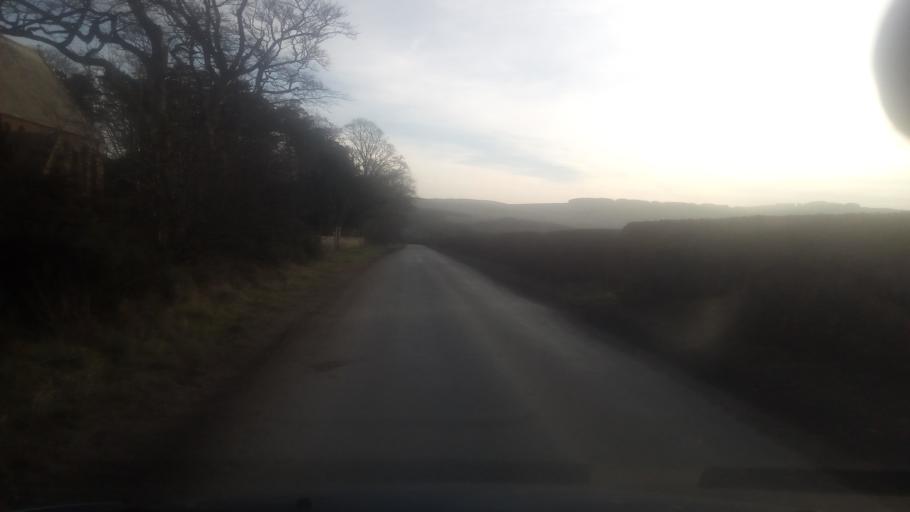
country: GB
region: Scotland
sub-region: The Scottish Borders
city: Jedburgh
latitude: 55.3911
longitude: -2.5950
